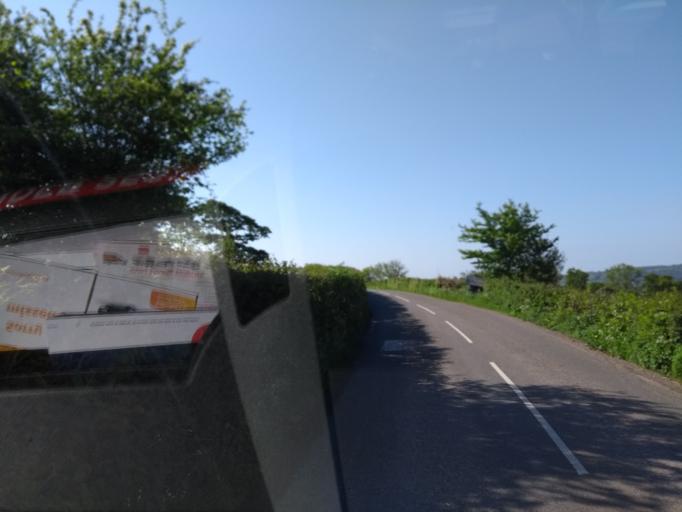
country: GB
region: England
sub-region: Devon
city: Colyton
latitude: 50.7677
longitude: -3.0658
